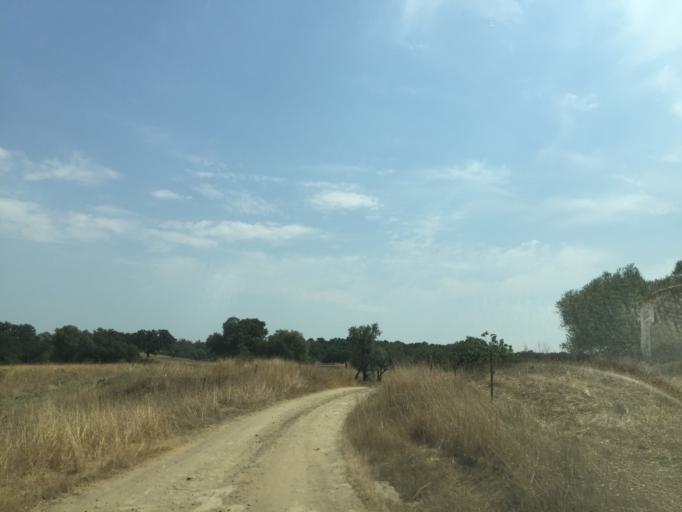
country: PT
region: Setubal
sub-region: Grandola
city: Grandola
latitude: 38.0330
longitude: -8.4849
